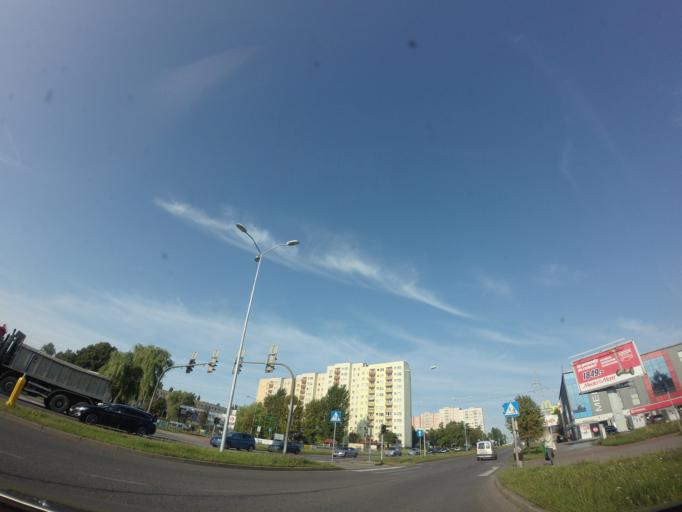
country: PL
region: West Pomeranian Voivodeship
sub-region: Szczecin
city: Szczecin
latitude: 53.4533
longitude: 14.5644
